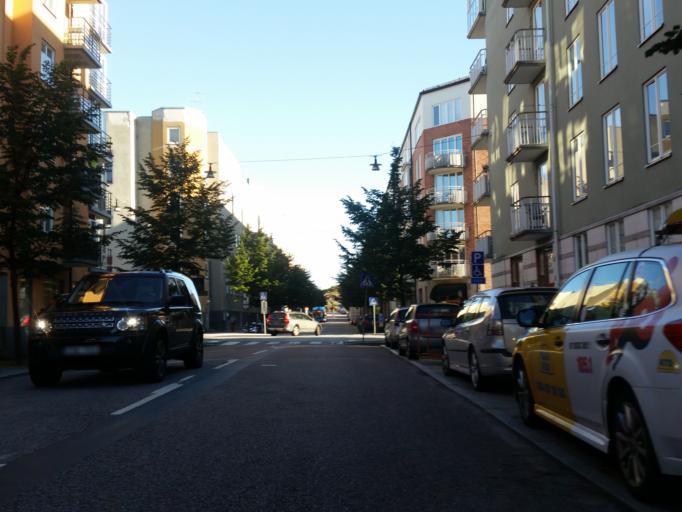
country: SE
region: Stockholm
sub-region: Stockholms Kommun
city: OEstermalm
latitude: 59.3103
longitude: 18.0980
